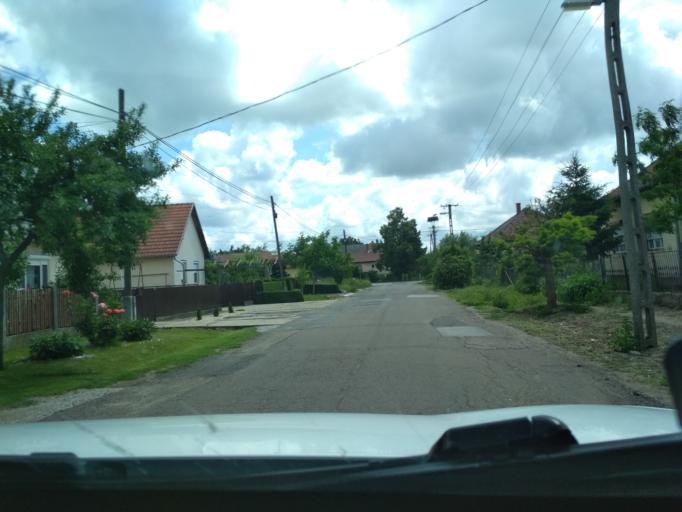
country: HU
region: Jasz-Nagykun-Szolnok
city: Tiszafured
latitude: 47.6088
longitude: 20.7526
